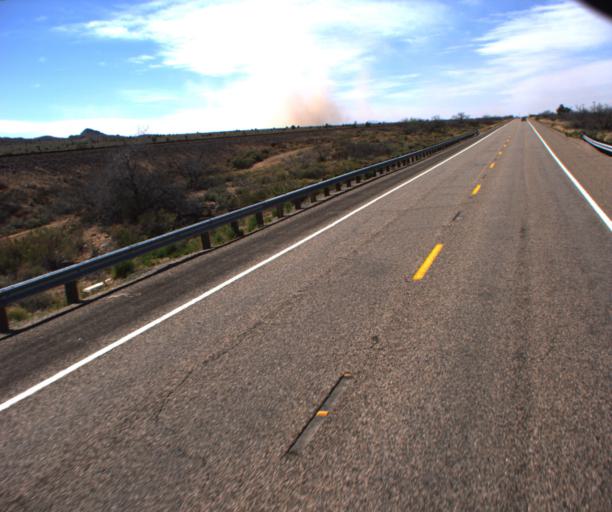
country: US
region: Arizona
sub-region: Mohave County
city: New Kingman-Butler
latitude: 35.4042
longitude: -113.7660
